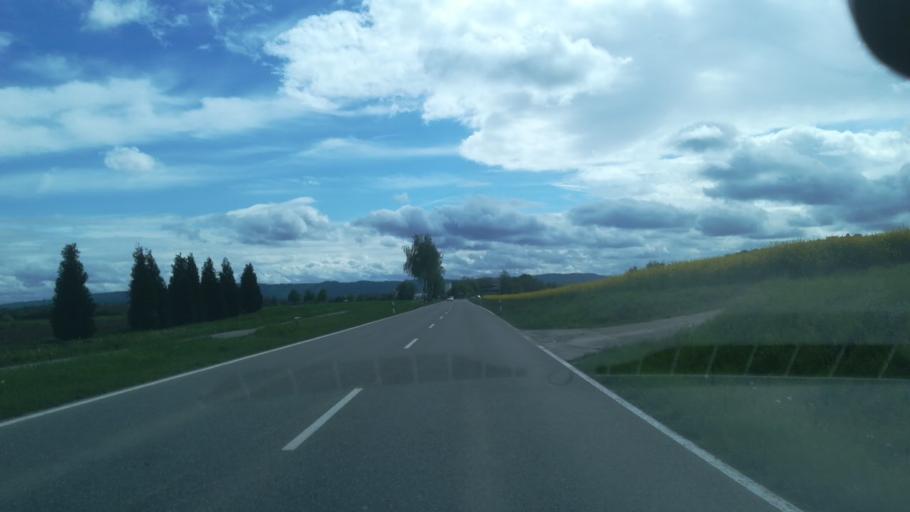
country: DE
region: Baden-Wuerttemberg
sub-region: Freiburg Region
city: Steisslingen
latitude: 47.7892
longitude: 8.9179
